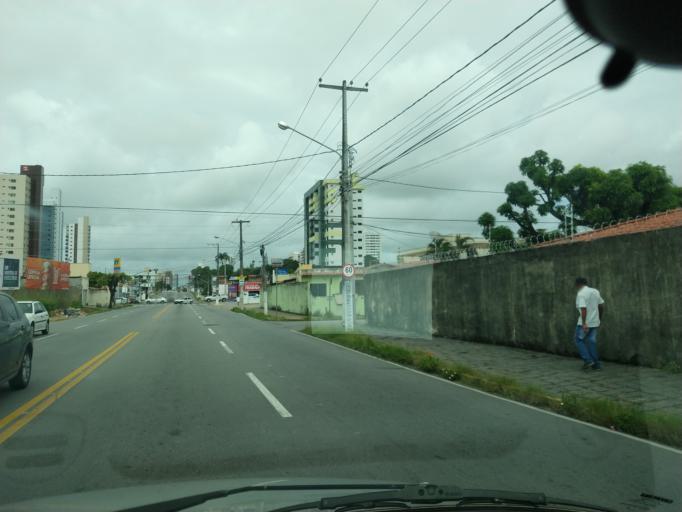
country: BR
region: Rio Grande do Norte
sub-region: Natal
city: Natal
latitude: -5.8163
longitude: -35.2175
